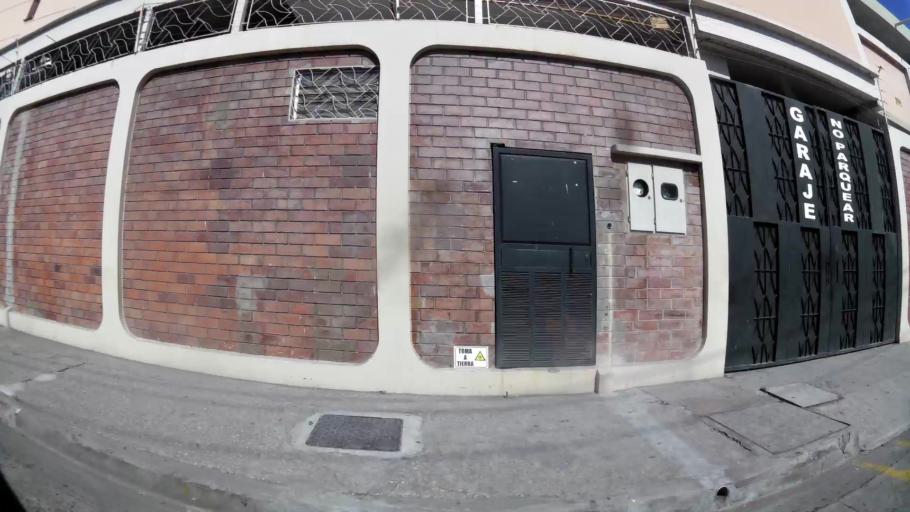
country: EC
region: Guayas
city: Guayaquil
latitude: -2.1667
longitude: -79.9076
